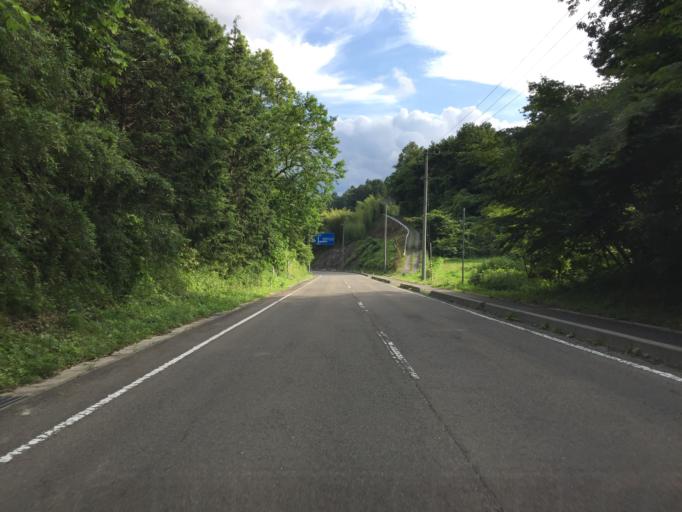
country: JP
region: Fukushima
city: Fukushima-shi
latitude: 37.6824
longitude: 140.5355
